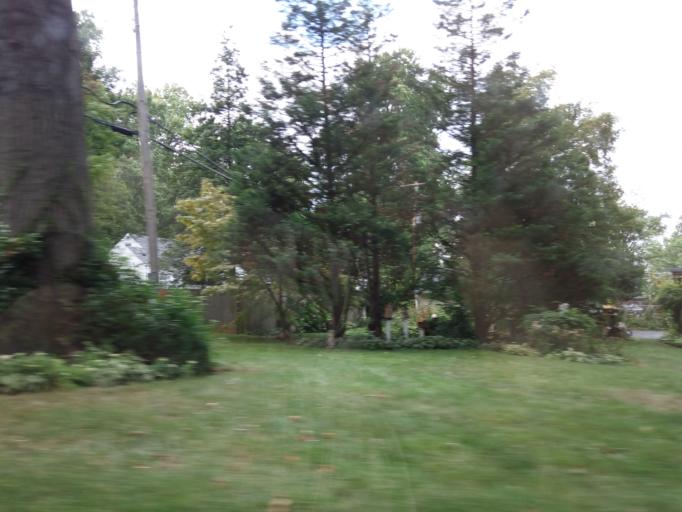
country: US
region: Kentucky
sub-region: Jefferson County
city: Audubon Park
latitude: 38.2087
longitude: -85.7215
